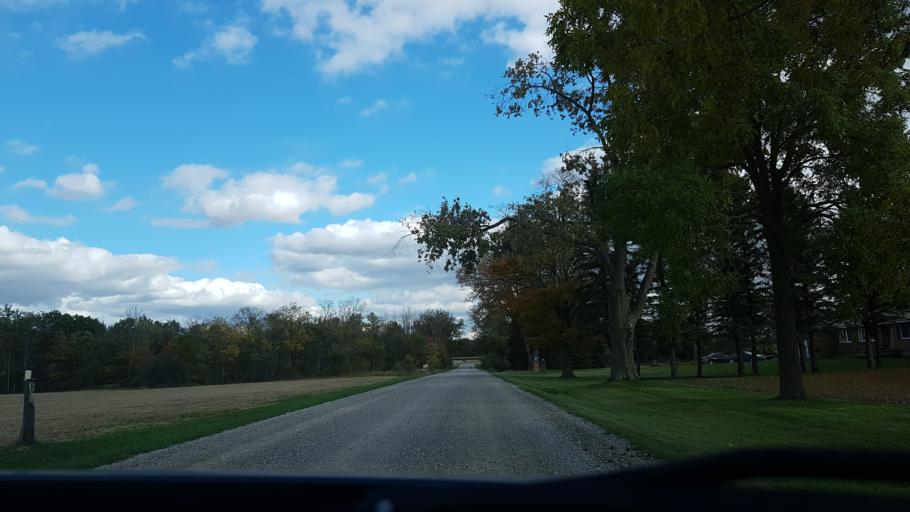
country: CA
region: Ontario
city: South Huron
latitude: 43.1069
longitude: -81.6132
